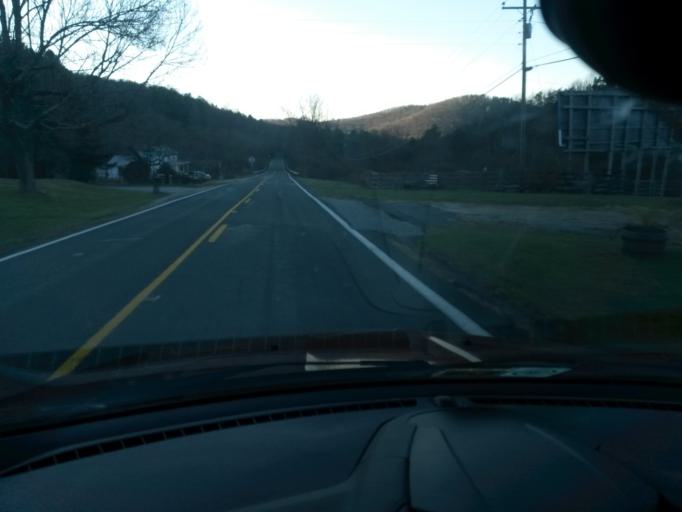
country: US
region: Virginia
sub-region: City of Buena Vista
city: Buena Vista
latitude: 37.7353
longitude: -79.2531
